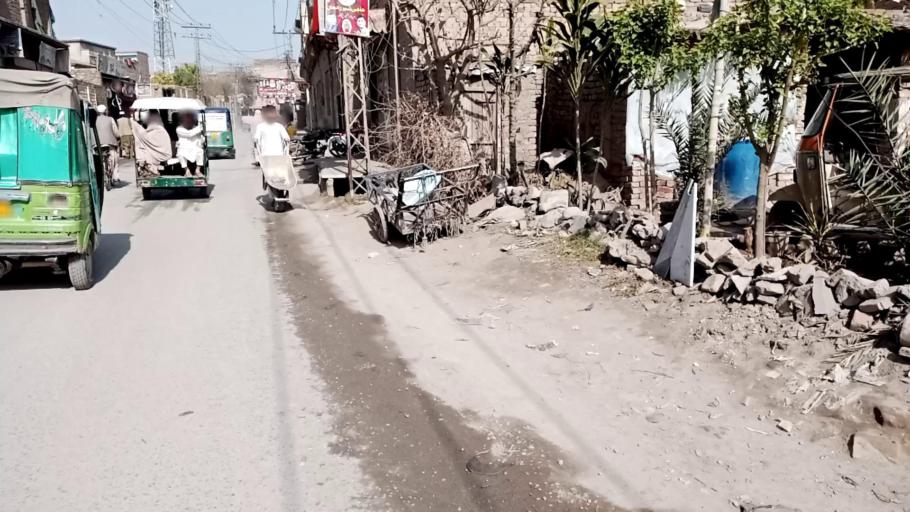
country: PK
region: Khyber Pakhtunkhwa
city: Peshawar
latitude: 33.9947
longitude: 71.5787
